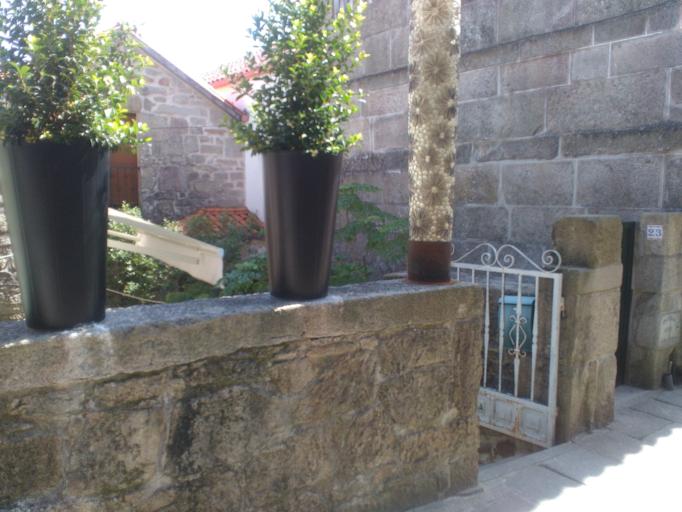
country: ES
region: Galicia
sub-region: Provincia de Pontevedra
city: Combarro
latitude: 42.4331
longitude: -8.7057
